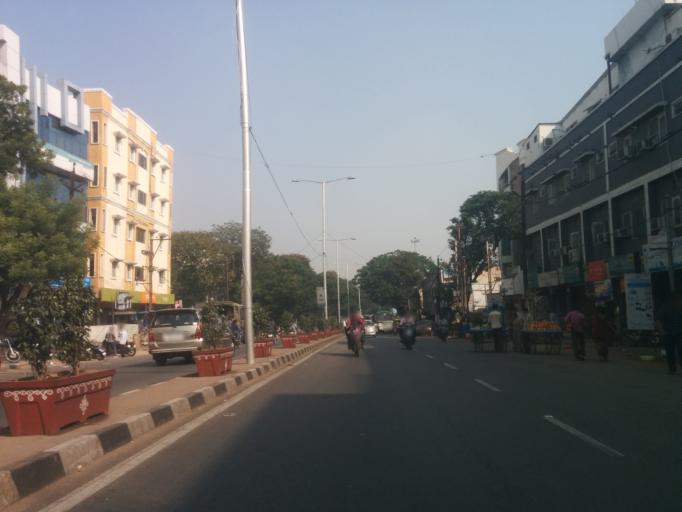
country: IN
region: Telangana
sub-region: Hyderabad
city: Hyderabad
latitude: 17.3941
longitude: 78.4270
